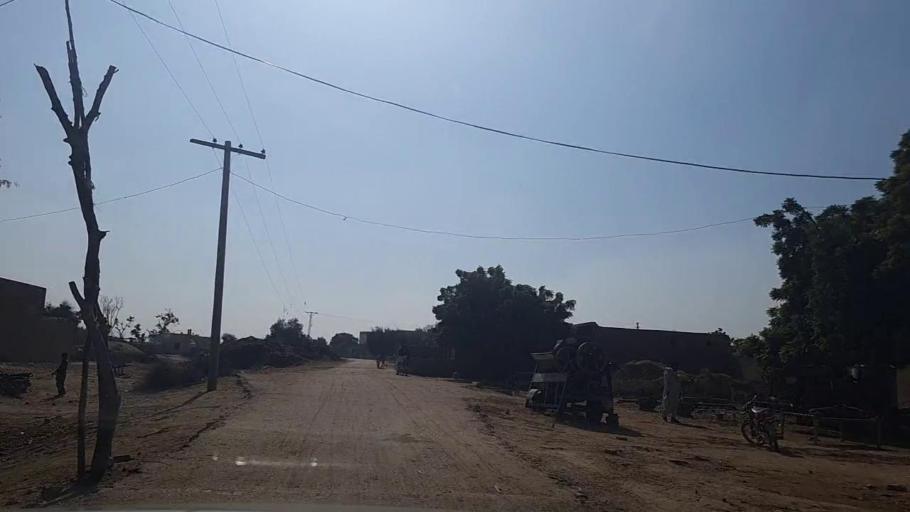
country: PK
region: Sindh
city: Sehwan
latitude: 26.2742
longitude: 68.0358
